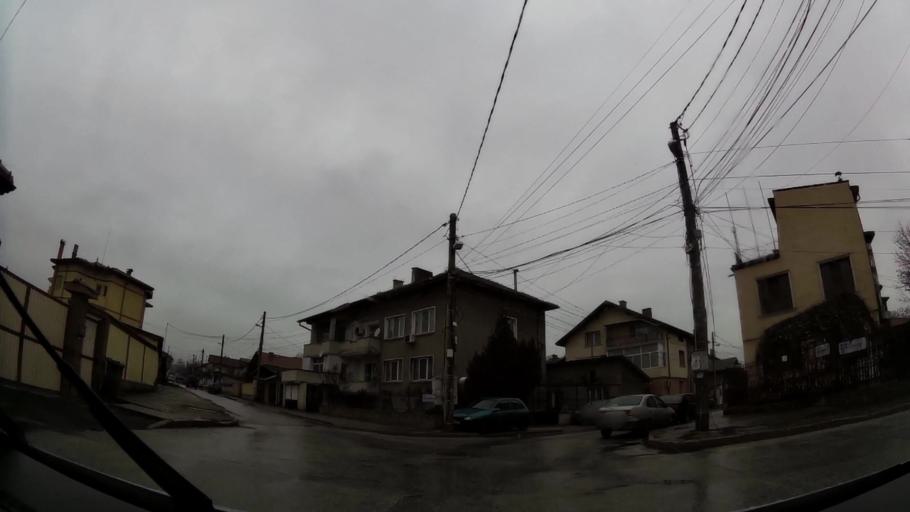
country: BG
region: Sofia-Capital
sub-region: Stolichna Obshtina
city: Sofia
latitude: 42.6241
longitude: 23.4025
